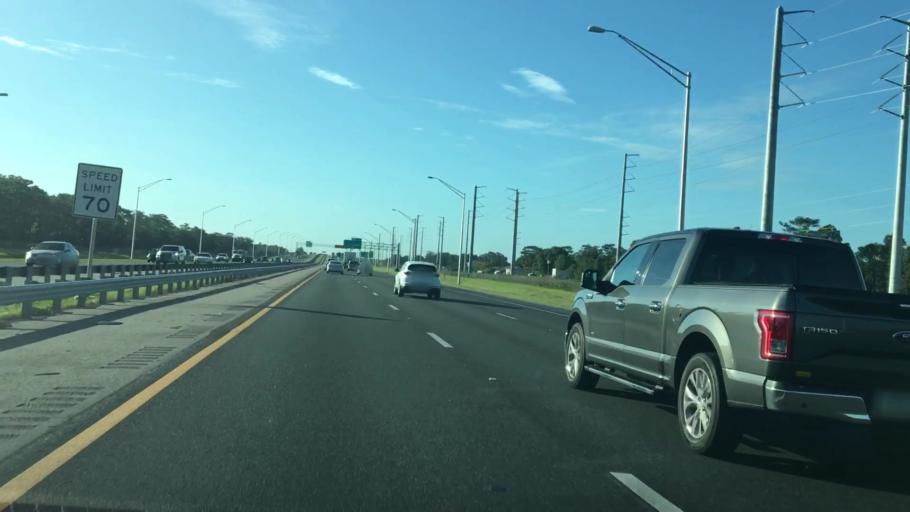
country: US
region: Florida
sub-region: Orange County
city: Azalea Park
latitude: 28.5316
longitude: -81.2510
